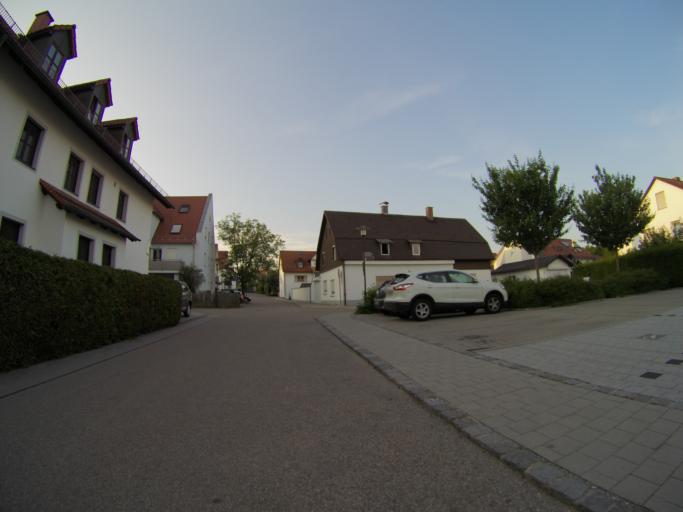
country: DE
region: Bavaria
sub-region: Upper Bavaria
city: Marzling
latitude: 48.4093
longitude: 11.7949
